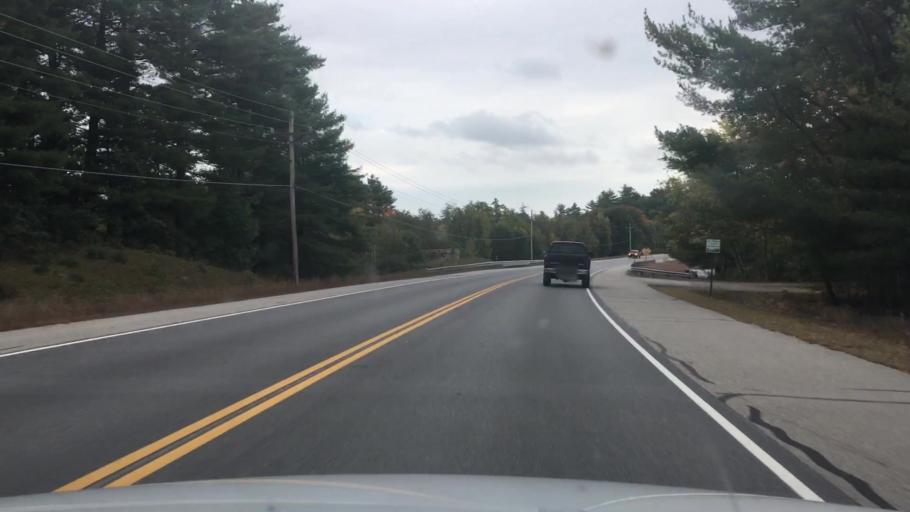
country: US
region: New Hampshire
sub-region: Strafford County
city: New Durham
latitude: 43.4341
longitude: -71.1713
